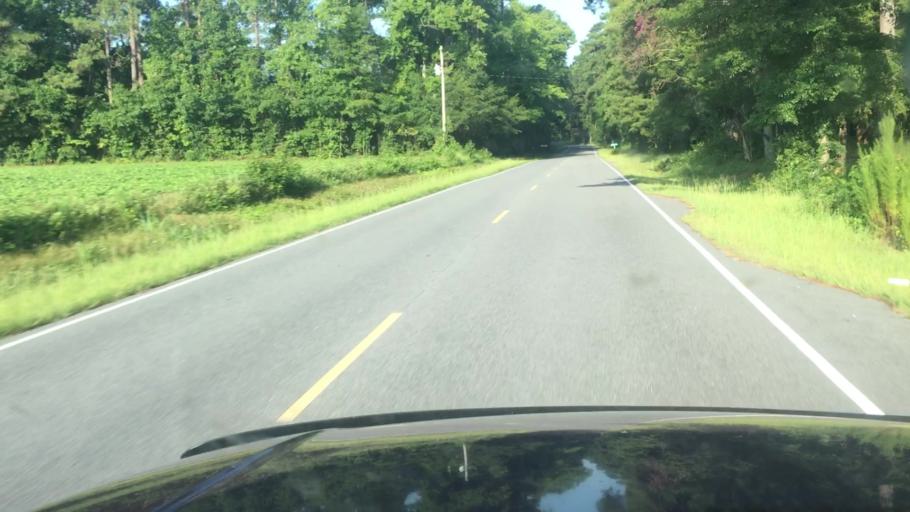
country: US
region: North Carolina
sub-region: Robeson County
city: Saint Pauls
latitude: 34.8340
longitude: -78.8991
